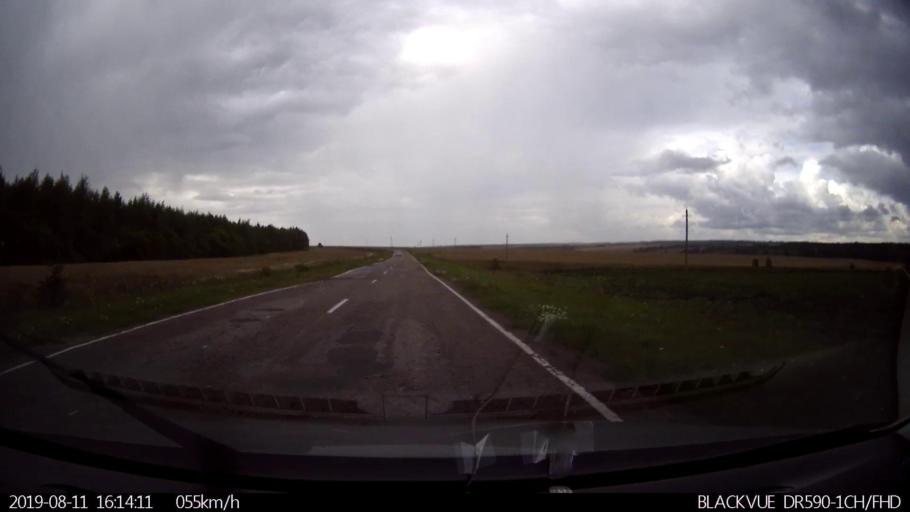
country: RU
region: Ulyanovsk
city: Ignatovka
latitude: 54.0260
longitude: 47.6347
